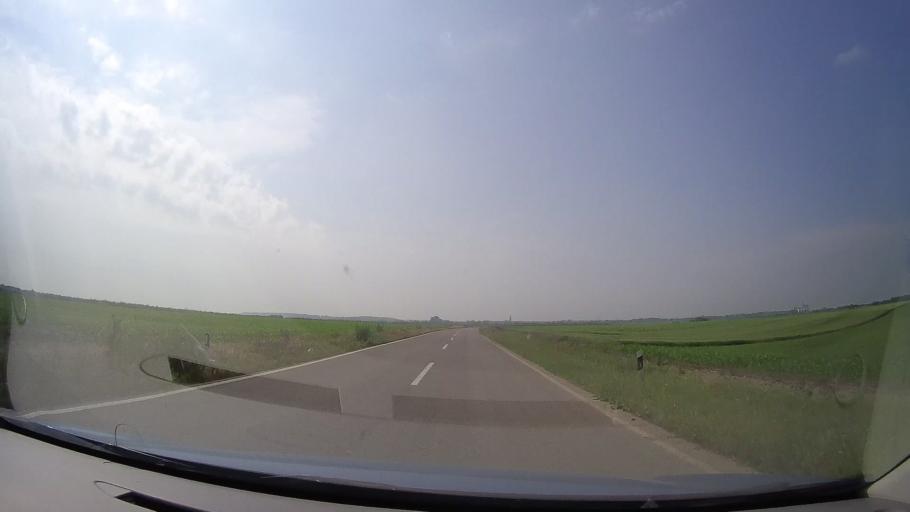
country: RS
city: Jasa Tomic
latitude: 45.4666
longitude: 20.8515
